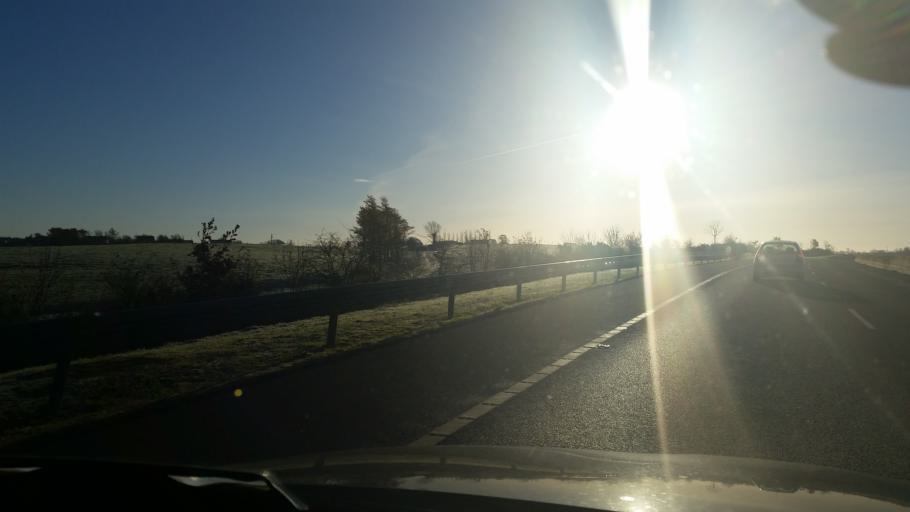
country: IE
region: Leinster
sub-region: Loch Garman
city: Gorey
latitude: 52.6800
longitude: -6.2593
